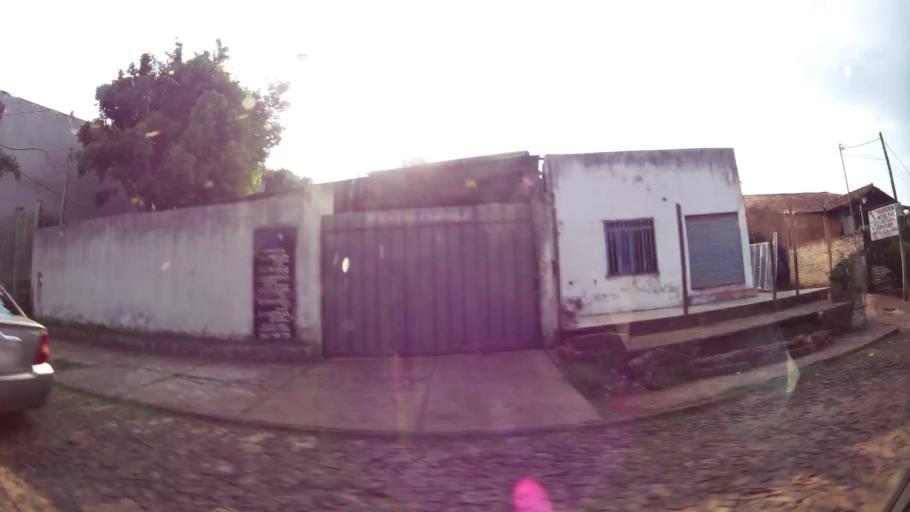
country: PY
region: Alto Parana
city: Presidente Franco
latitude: -25.5258
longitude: -54.6283
